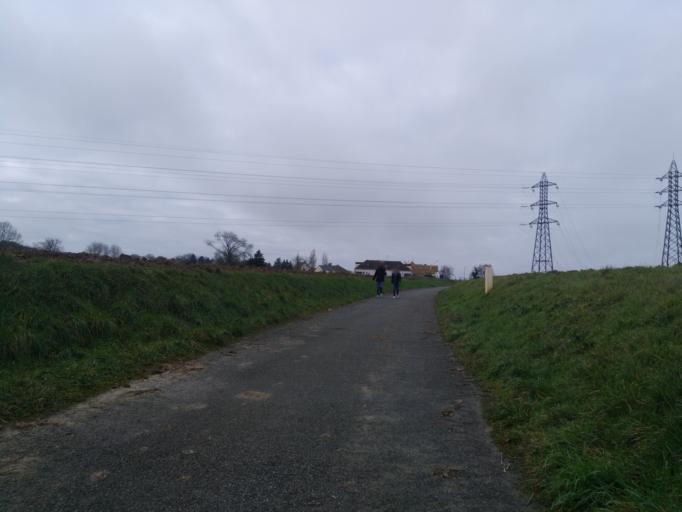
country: FR
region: Ile-de-France
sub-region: Departement des Yvelines
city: Plaisir
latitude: 48.8199
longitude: 1.9385
